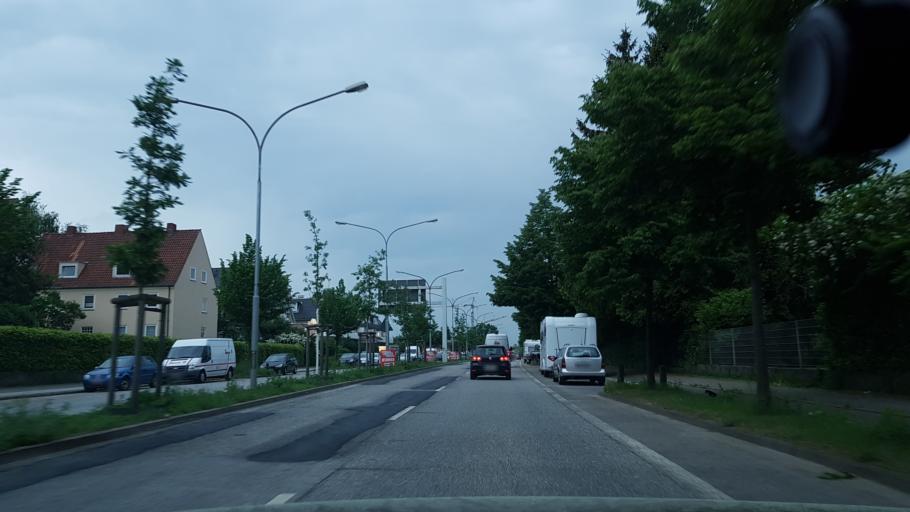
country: DE
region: Schleswig-Holstein
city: Luebeck
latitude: 53.8516
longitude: 10.6969
